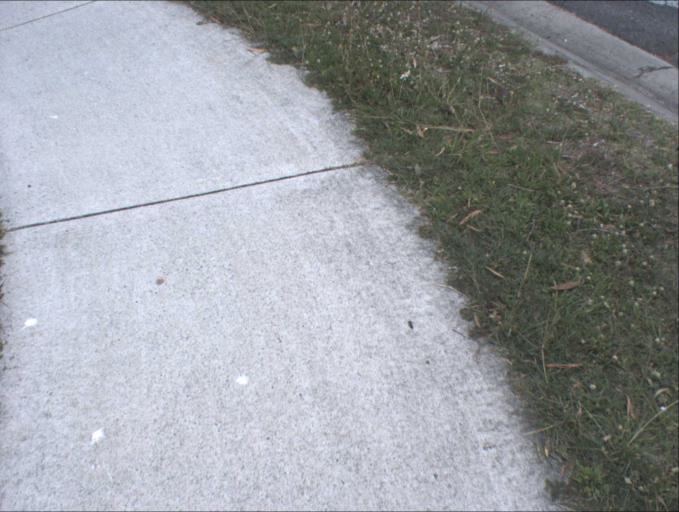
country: AU
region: Queensland
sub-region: Logan
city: Park Ridge South
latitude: -27.6701
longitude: 153.0455
